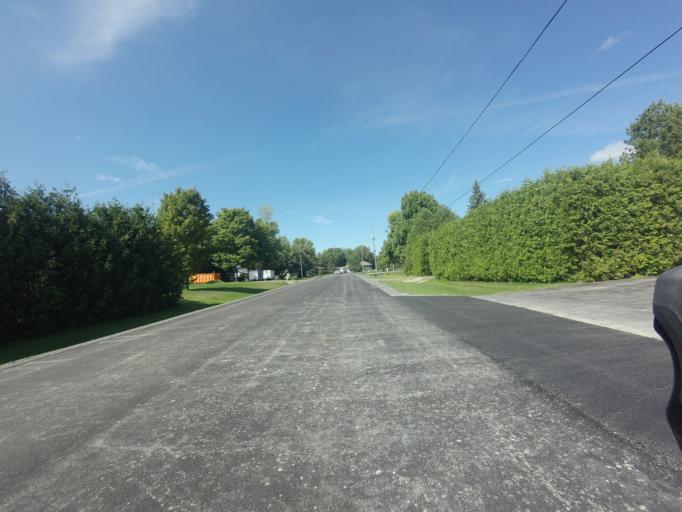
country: CA
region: Ontario
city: Carleton Place
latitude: 45.1332
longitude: -76.0657
